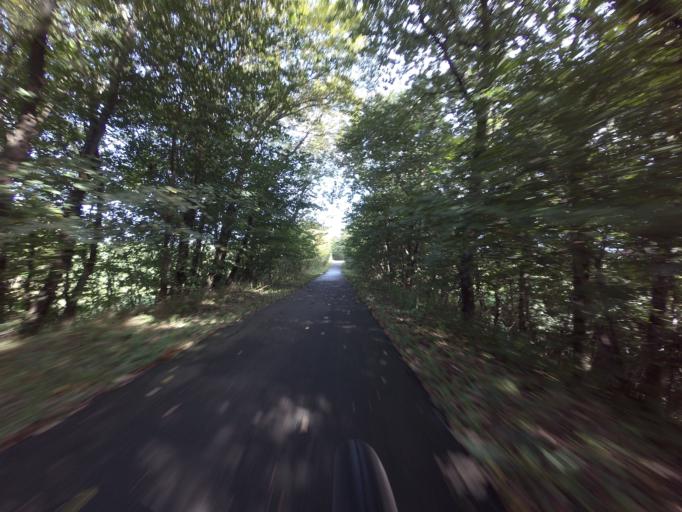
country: DK
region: Central Jutland
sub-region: Viborg Kommune
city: Bjerringbro
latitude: 56.4598
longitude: 9.5866
